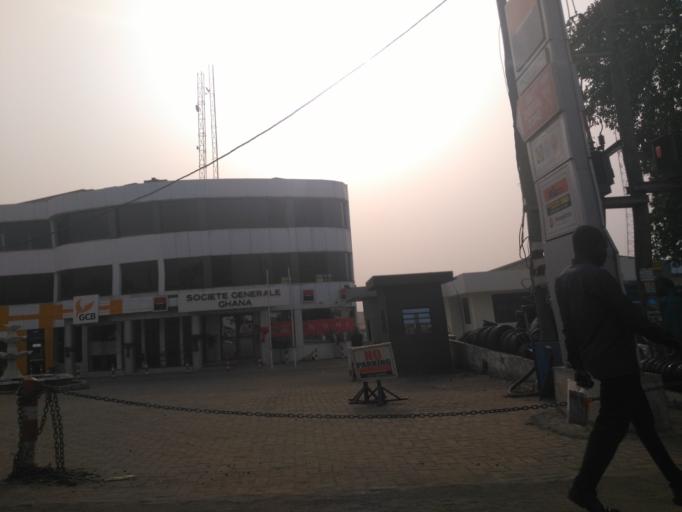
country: GH
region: Ashanti
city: Tafo
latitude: 6.7190
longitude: -1.6316
